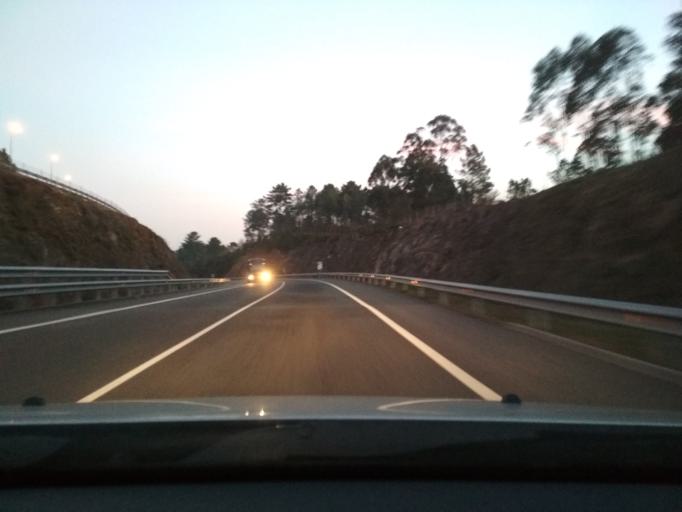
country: ES
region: Galicia
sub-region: Provincia da Coruna
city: Santiago de Compostela
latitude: 42.8391
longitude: -8.5929
